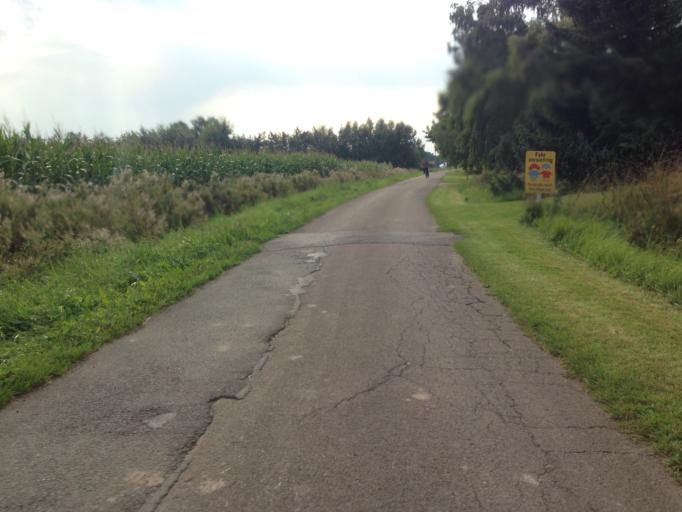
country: DE
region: North Rhine-Westphalia
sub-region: Regierungsbezirk Munster
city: Greven
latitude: 52.0227
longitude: 7.5560
